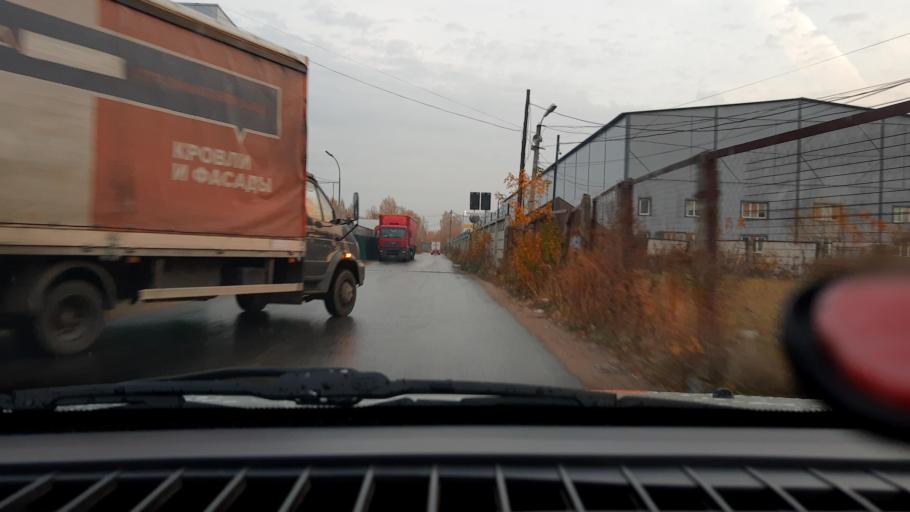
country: RU
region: Nizjnij Novgorod
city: Gorbatovka
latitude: 56.3177
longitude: 43.8515
